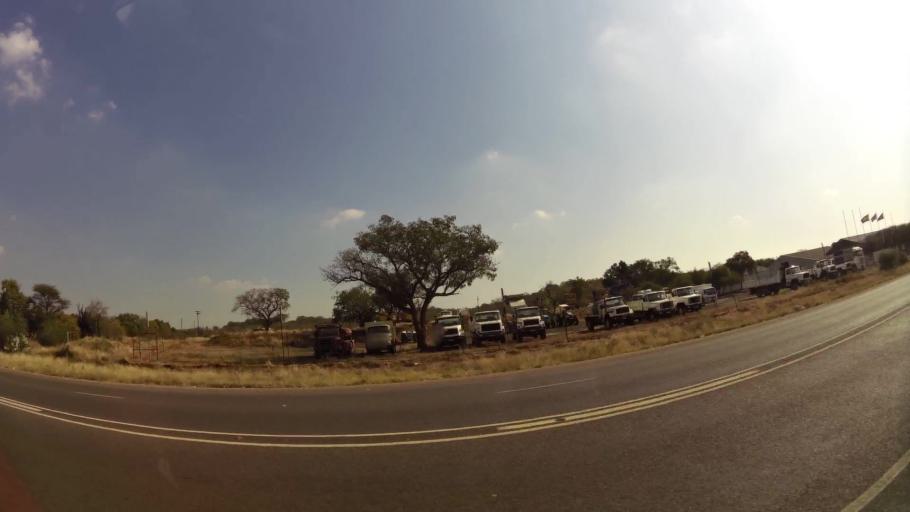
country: ZA
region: North-West
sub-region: Bojanala Platinum District Municipality
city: Mogwase
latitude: -25.4478
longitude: 27.0880
